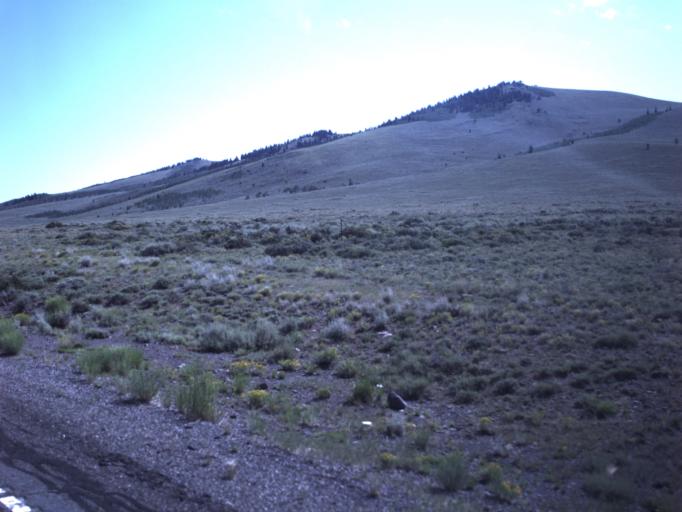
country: US
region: Utah
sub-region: Wayne County
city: Loa
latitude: 38.5539
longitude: -111.5076
